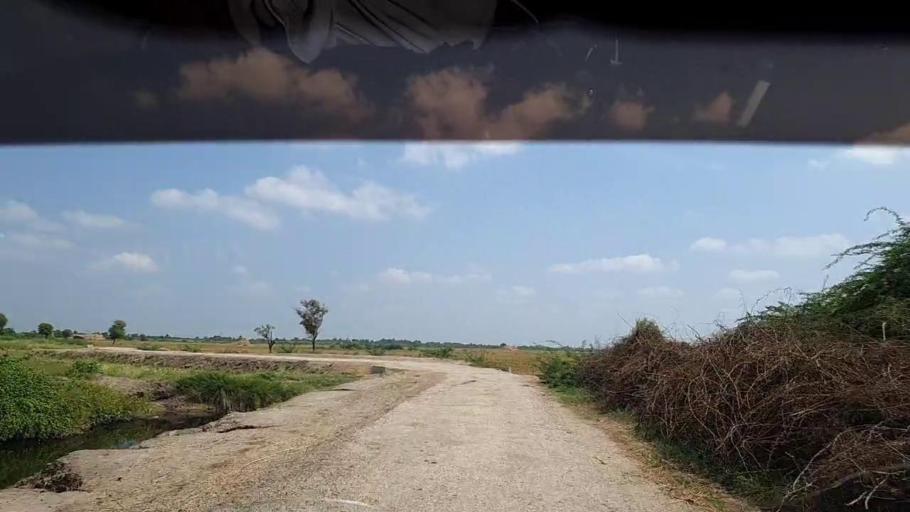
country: PK
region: Sindh
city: Kadhan
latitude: 24.5824
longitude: 68.9642
